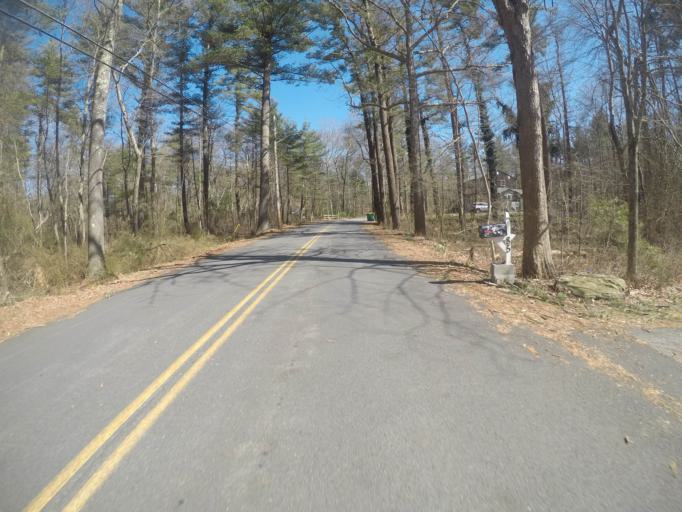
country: US
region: Massachusetts
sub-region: Bristol County
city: Easton
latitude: 41.9976
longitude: -71.1125
